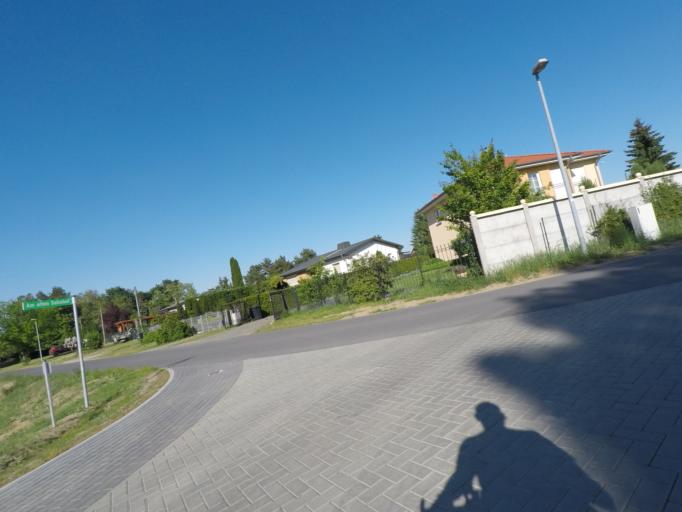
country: DE
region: Brandenburg
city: Melchow
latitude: 52.8406
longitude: 13.6764
